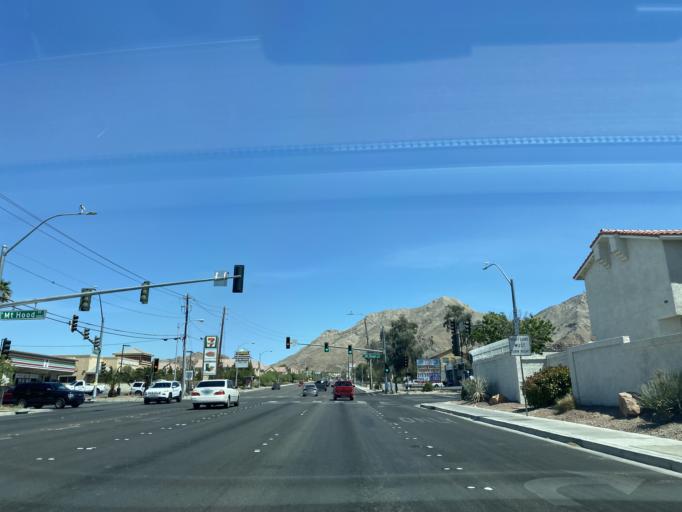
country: US
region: Nevada
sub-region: Clark County
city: Sunrise Manor
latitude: 36.1959
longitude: -115.0361
